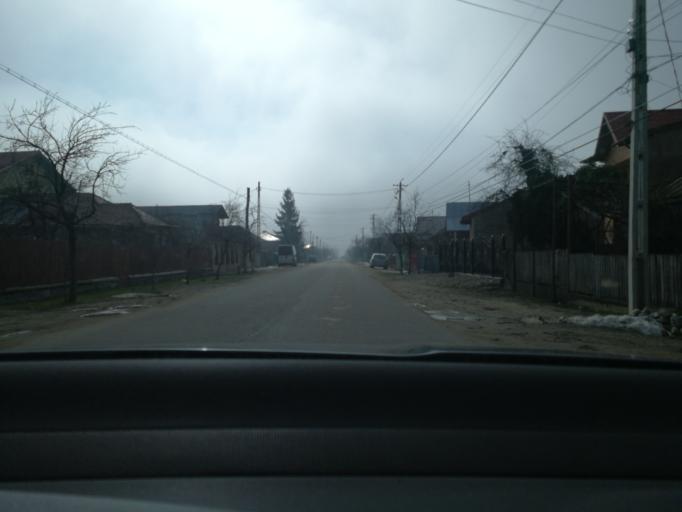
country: RO
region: Prahova
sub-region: Comuna Magureni
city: Lunca Prahovei
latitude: 45.0383
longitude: 25.7576
